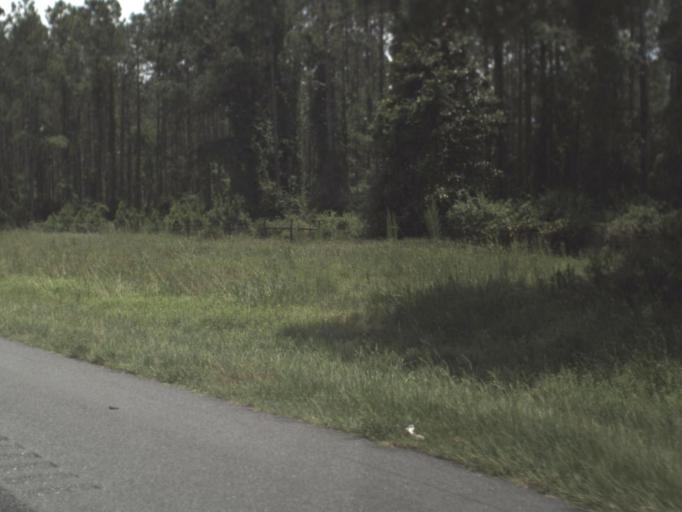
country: US
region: Florida
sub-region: Hamilton County
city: Jasper
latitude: 30.4629
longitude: -82.9567
